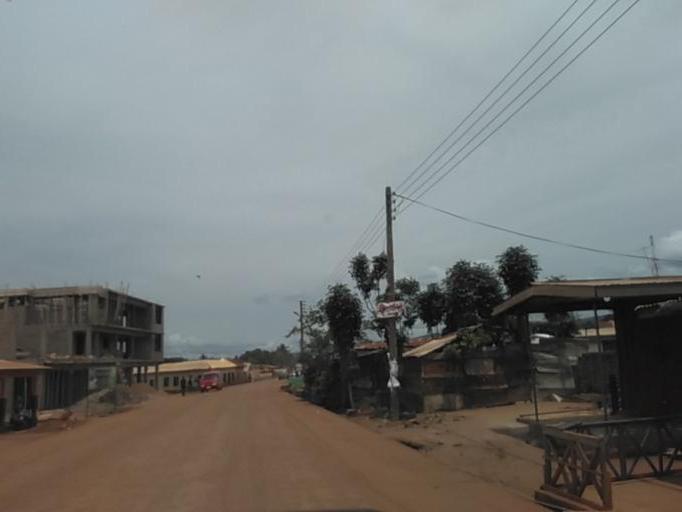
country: GH
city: Akropong
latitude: 6.1366
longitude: 0.0049
